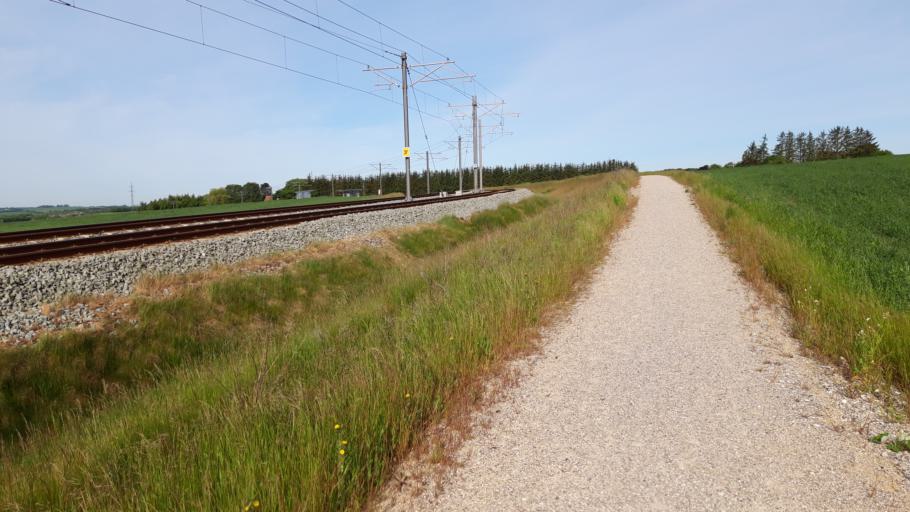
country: DK
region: Central Jutland
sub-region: Arhus Kommune
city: Lystrup
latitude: 56.2276
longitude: 10.2034
